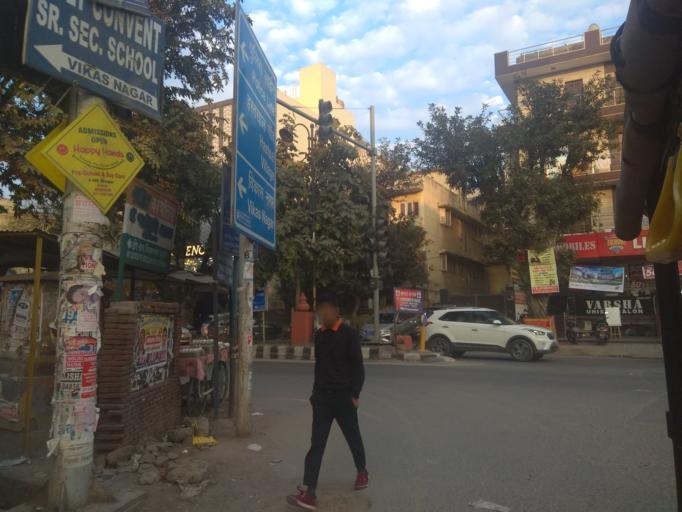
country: IN
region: NCT
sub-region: West Delhi
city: Nangloi Jat
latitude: 28.6344
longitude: 77.0687
